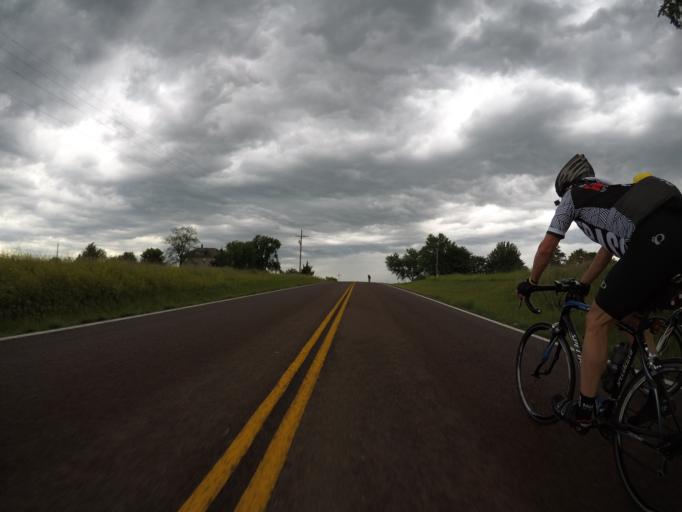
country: US
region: Kansas
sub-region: Shawnee County
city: Rossville
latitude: 38.9645
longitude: -96.0120
